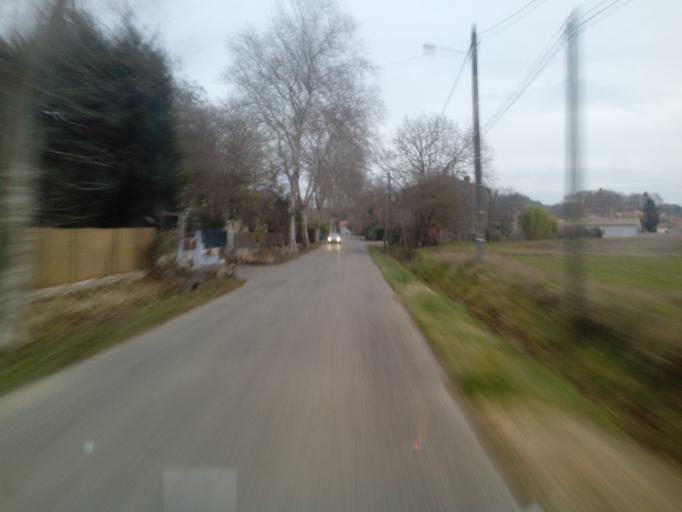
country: FR
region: Midi-Pyrenees
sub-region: Departement de l'Ariege
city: Mazeres
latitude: 43.2469
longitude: 1.7131
